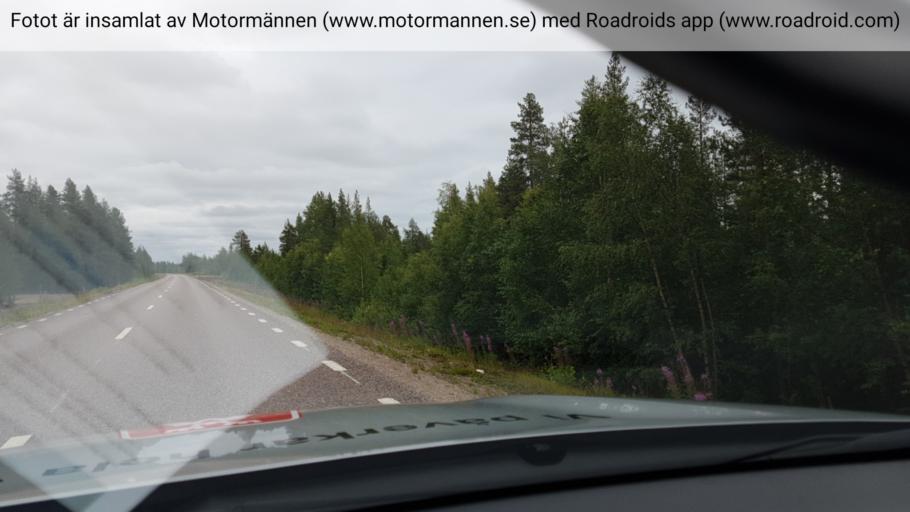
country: SE
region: Norrbotten
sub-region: Gallivare Kommun
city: Gaellivare
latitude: 67.0751
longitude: 21.3608
